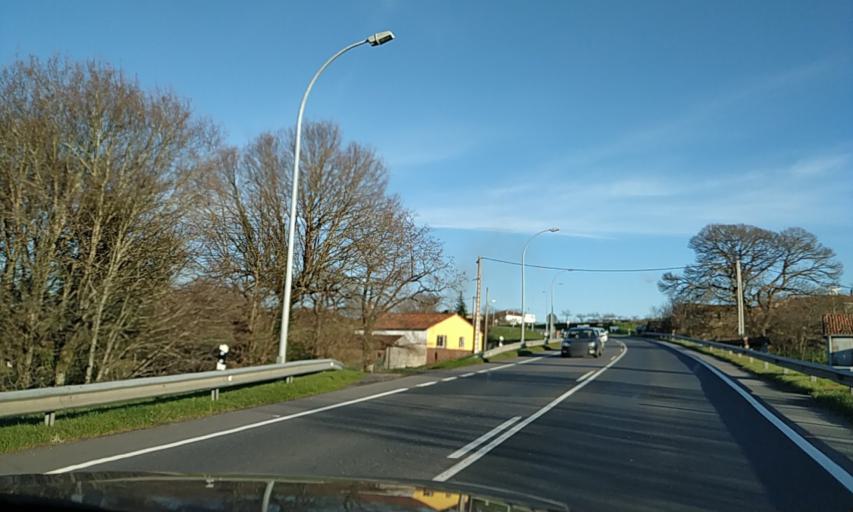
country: ES
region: Galicia
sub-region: Provincia de Pontevedra
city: Silleda
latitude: 42.6840
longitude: -8.1976
